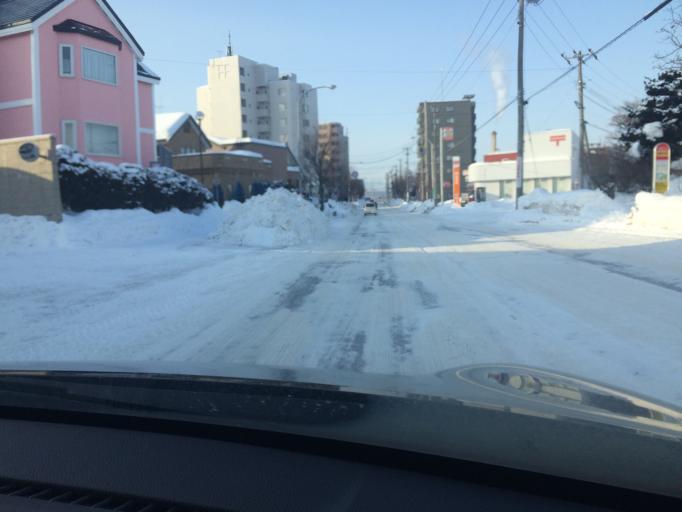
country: JP
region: Hokkaido
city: Ebetsu
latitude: 43.0448
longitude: 141.4840
